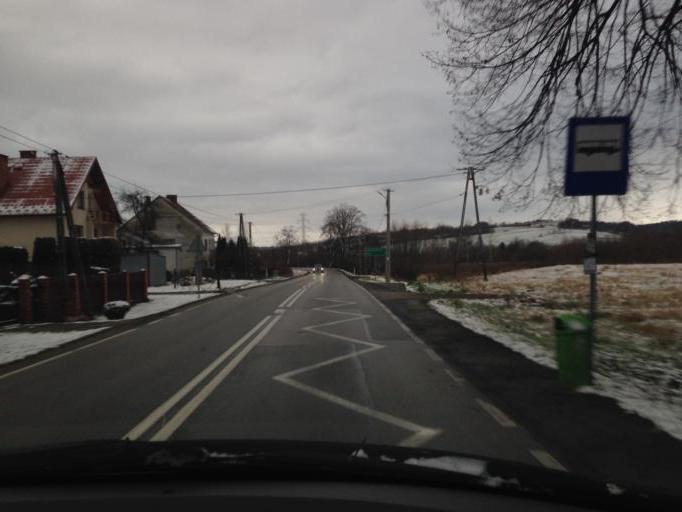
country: PL
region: Lesser Poland Voivodeship
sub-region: Powiat tarnowski
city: Gromnik
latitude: 49.8414
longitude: 20.9765
